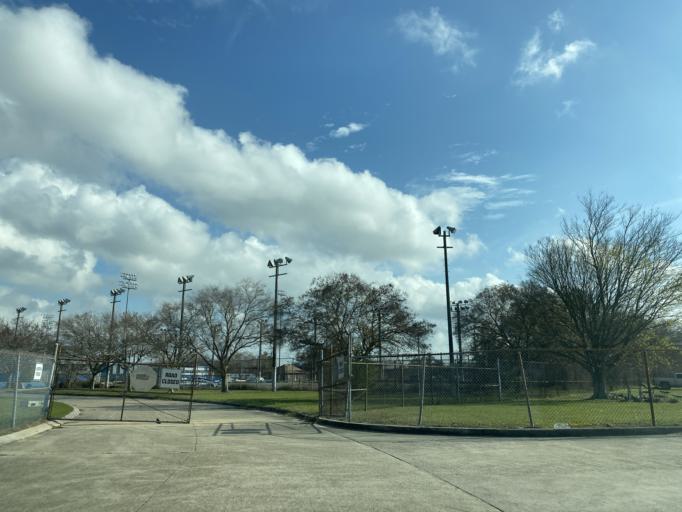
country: US
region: Louisiana
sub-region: Orleans Parish
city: New Orleans
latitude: 30.0313
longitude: -90.0492
